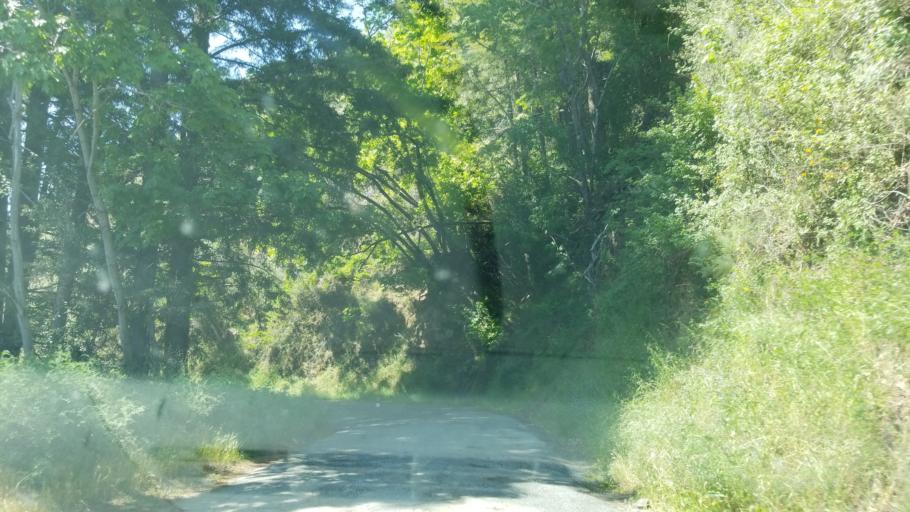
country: US
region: California
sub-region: Santa Cruz County
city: Day Valley
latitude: 37.0622
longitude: -121.8251
